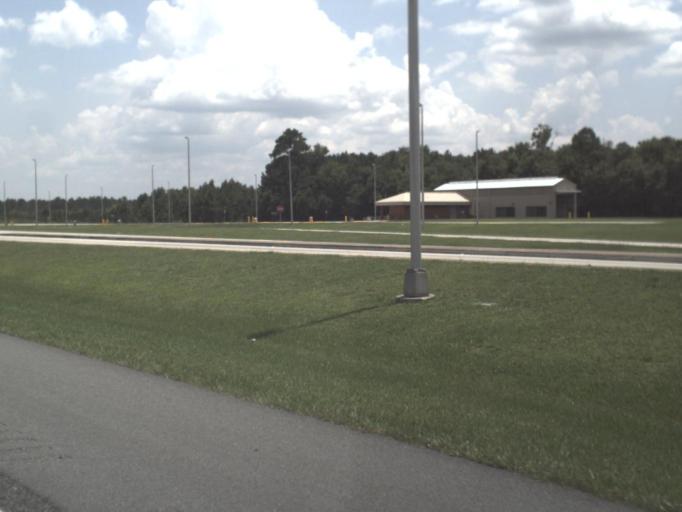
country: US
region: Florida
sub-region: Hamilton County
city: Jasper
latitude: 30.4239
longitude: -82.9043
